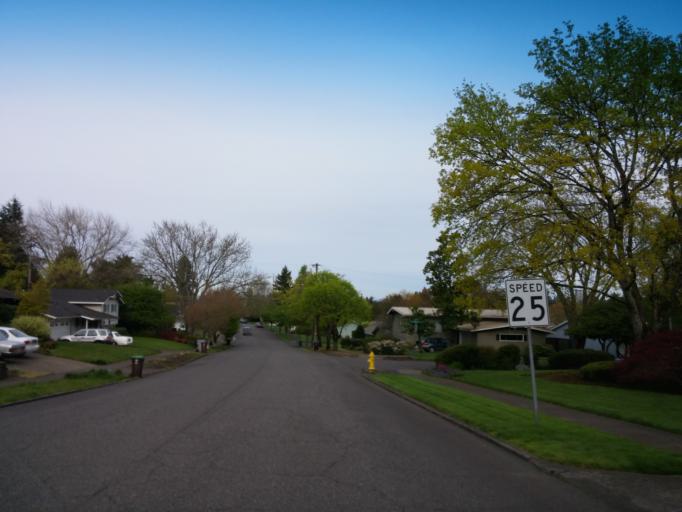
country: US
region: Oregon
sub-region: Washington County
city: Cedar Hills
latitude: 45.5091
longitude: -122.8080
